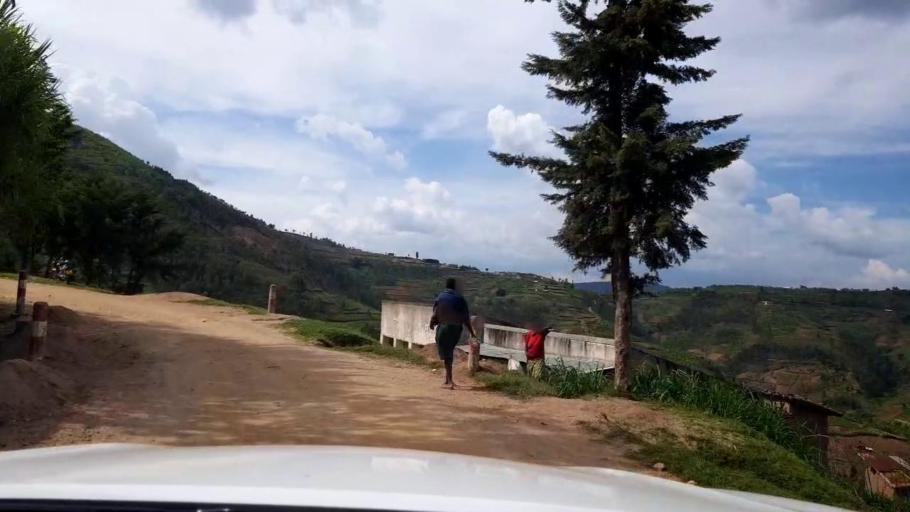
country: RW
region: Southern Province
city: Gitarama
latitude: -1.9946
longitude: 29.7122
